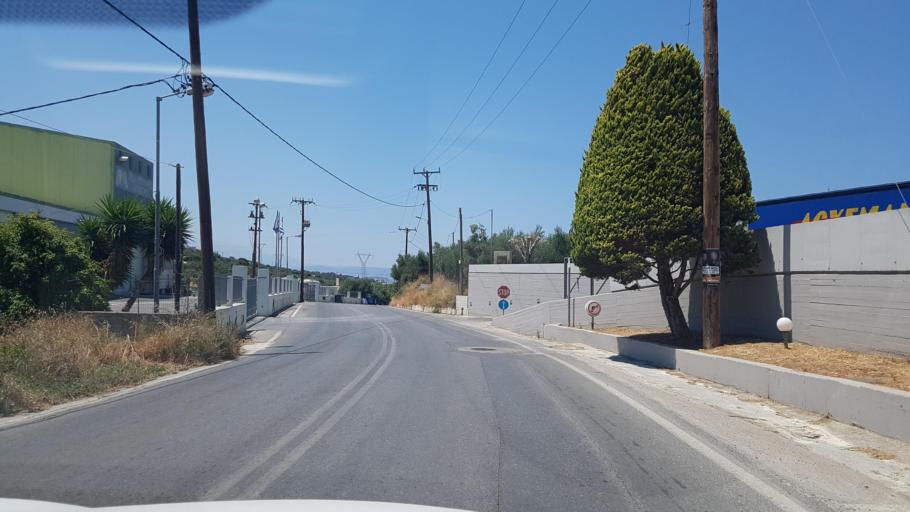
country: GR
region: Crete
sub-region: Nomos Rethymnis
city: Rethymno
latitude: 35.3590
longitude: 24.5515
